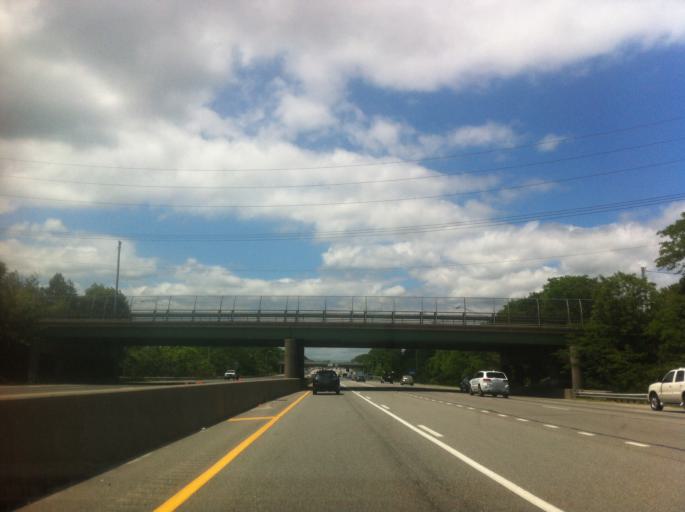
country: US
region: New York
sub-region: Suffolk County
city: Ronkonkoma
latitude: 40.8138
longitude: -73.1058
